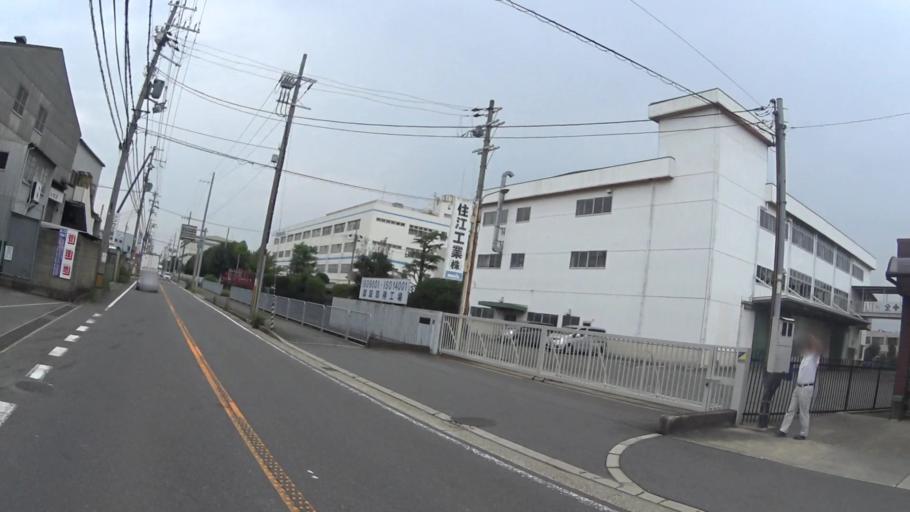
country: JP
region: Kyoto
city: Tanabe
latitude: 34.8418
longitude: 135.7505
